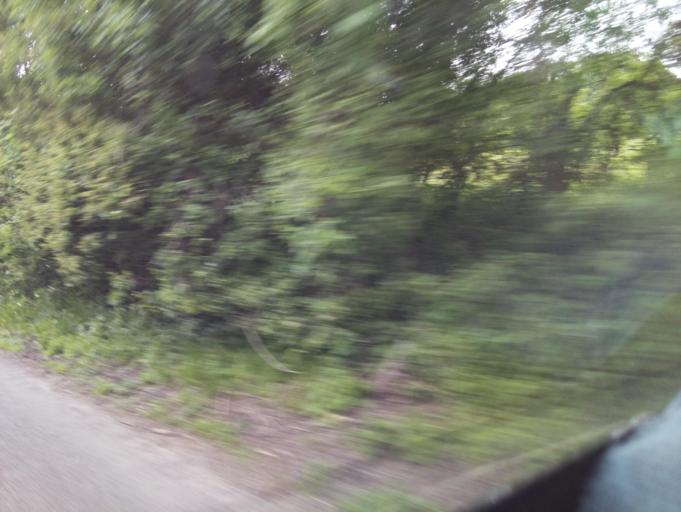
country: GB
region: England
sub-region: Worcestershire
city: Great Malvern
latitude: 52.1378
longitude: -2.3592
